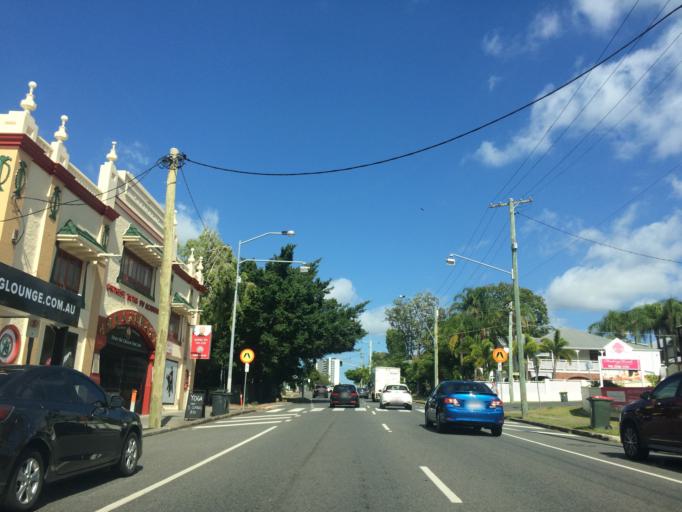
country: AU
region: Queensland
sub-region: Brisbane
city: Woolloongabba
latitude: -27.4882
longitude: 153.0469
